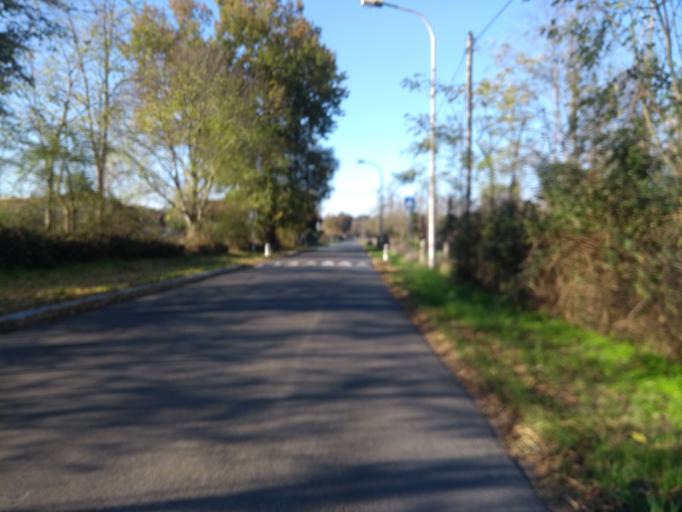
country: FR
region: Aquitaine
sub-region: Departement de la Gironde
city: Martillac
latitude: 44.7223
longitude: -0.5096
